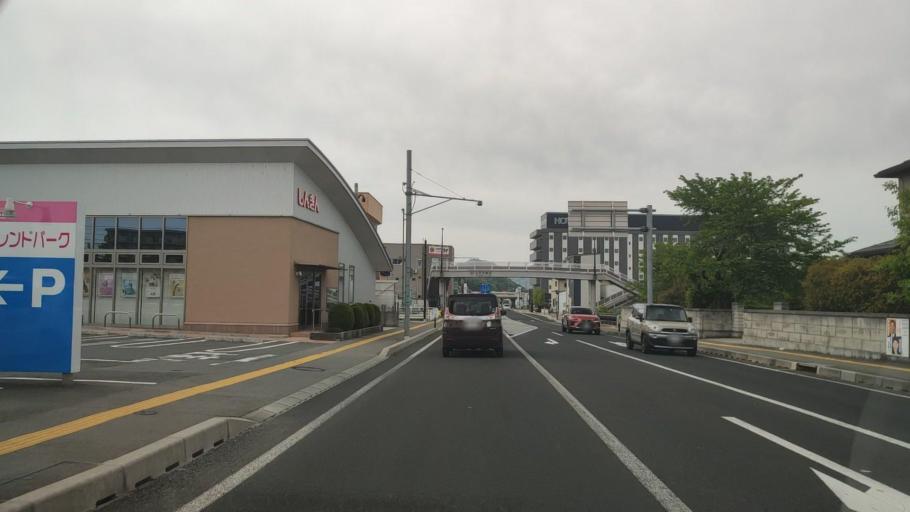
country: JP
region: Yamagata
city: Yamagata-shi
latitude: 38.2183
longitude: 140.3240
